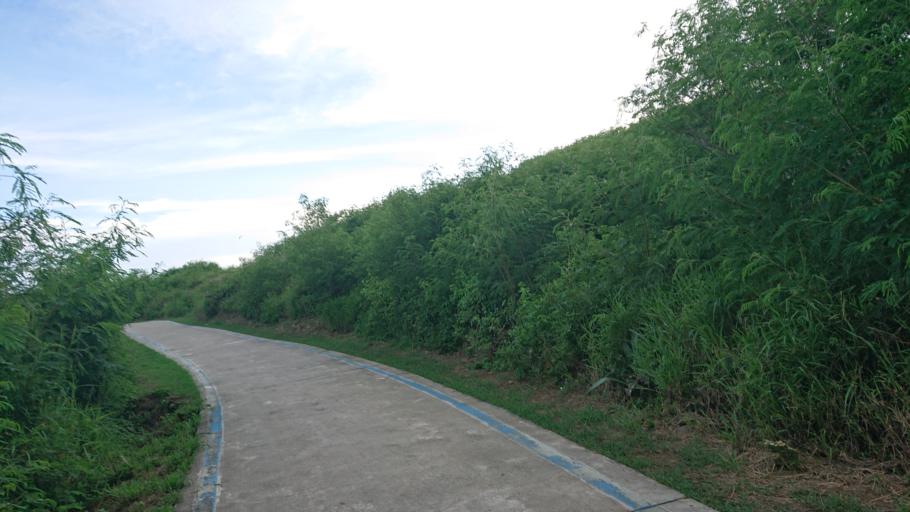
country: TW
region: Taiwan
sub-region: Penghu
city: Ma-kung
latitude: 23.5169
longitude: 119.6055
